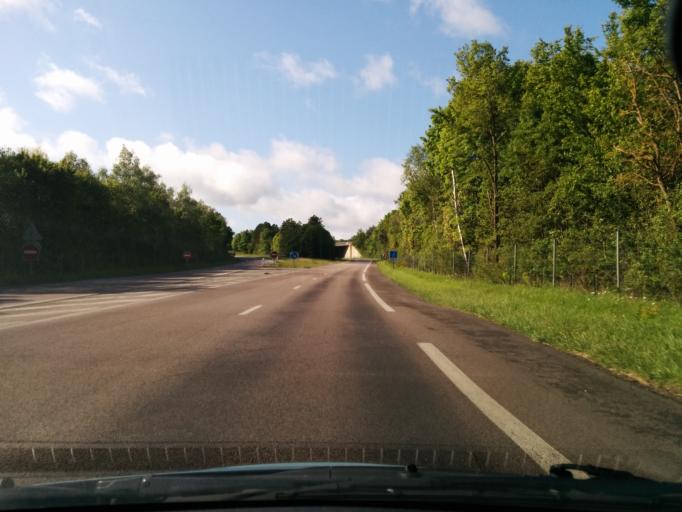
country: FR
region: Ile-de-France
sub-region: Departement des Yvelines
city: Bonnieres-sur-Seine
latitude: 49.0200
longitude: 1.5868
